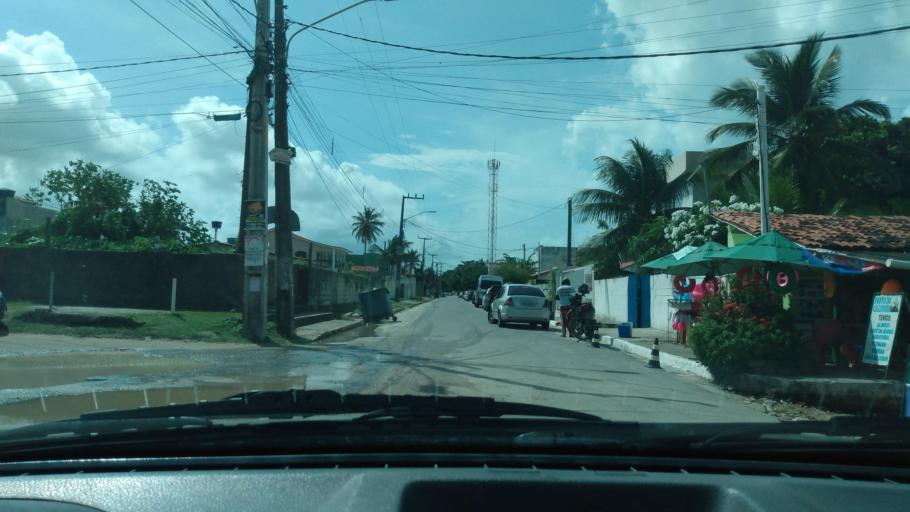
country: BR
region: Pernambuco
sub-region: Cabo De Santo Agostinho
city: Cabo
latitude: -8.3366
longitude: -34.9514
